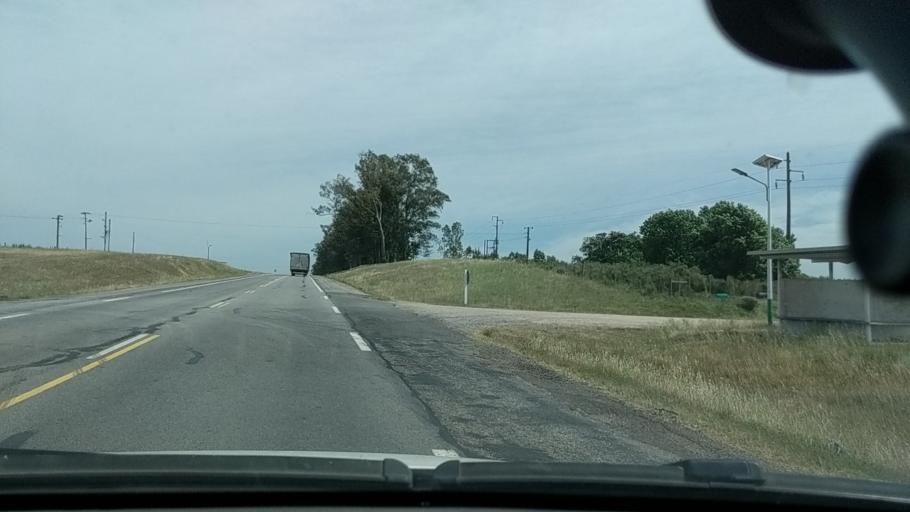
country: UY
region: Durazno
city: Durazno
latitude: -33.5188
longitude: -56.4083
